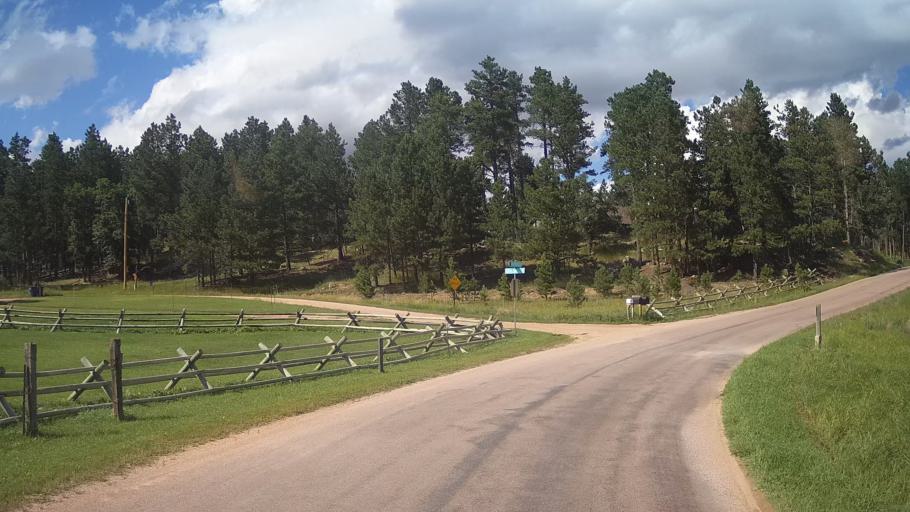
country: US
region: South Dakota
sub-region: Pennington County
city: Colonial Pine Hills
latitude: 43.8482
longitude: -103.3837
